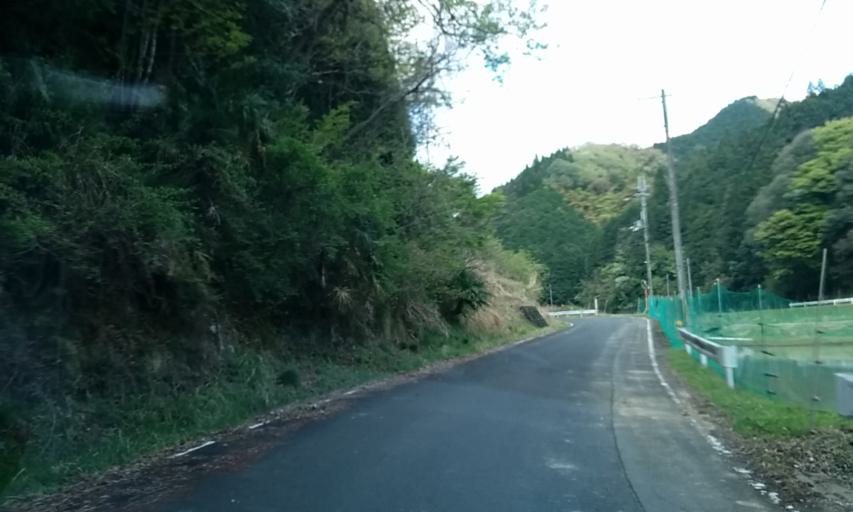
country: JP
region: Kyoto
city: Ayabe
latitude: 35.2481
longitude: 135.3007
